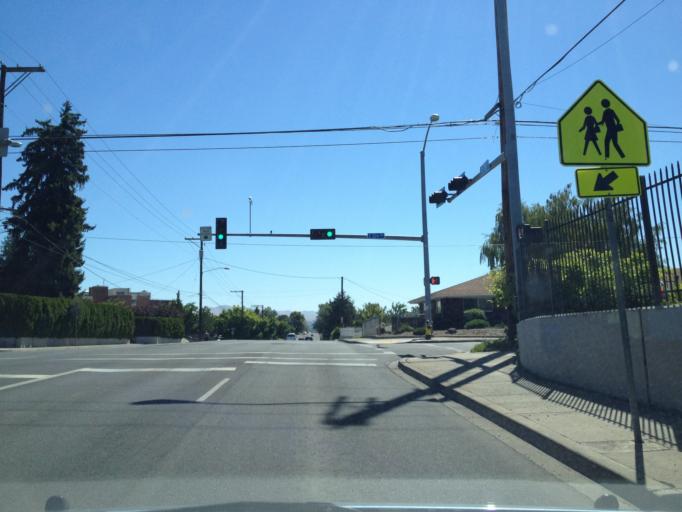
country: US
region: Washington
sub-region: Yakima County
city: Yakima
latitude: 46.5927
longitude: -120.5519
